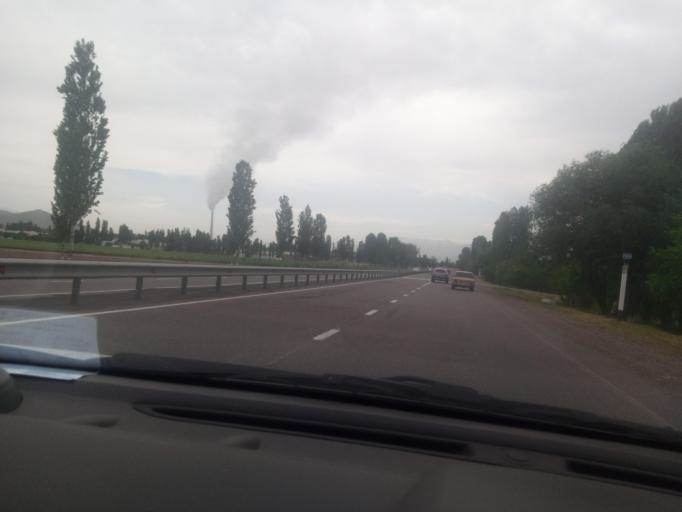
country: UZ
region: Toshkent
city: Ohangaron
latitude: 40.9090
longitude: 69.7596
